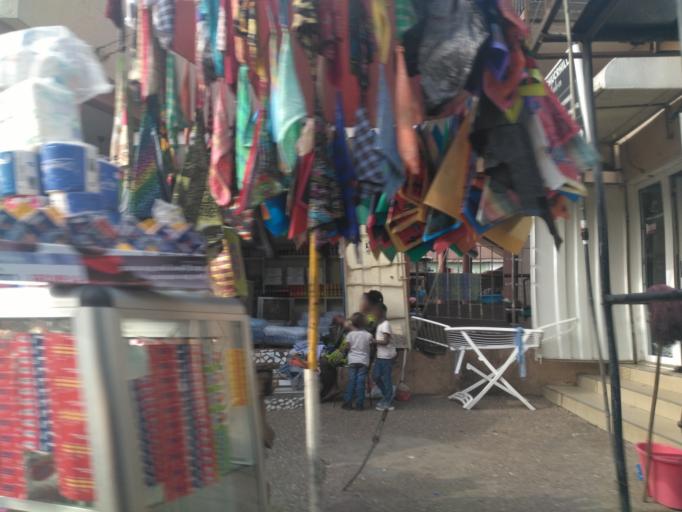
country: GH
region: Ashanti
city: Kumasi
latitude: 6.6874
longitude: -1.6123
